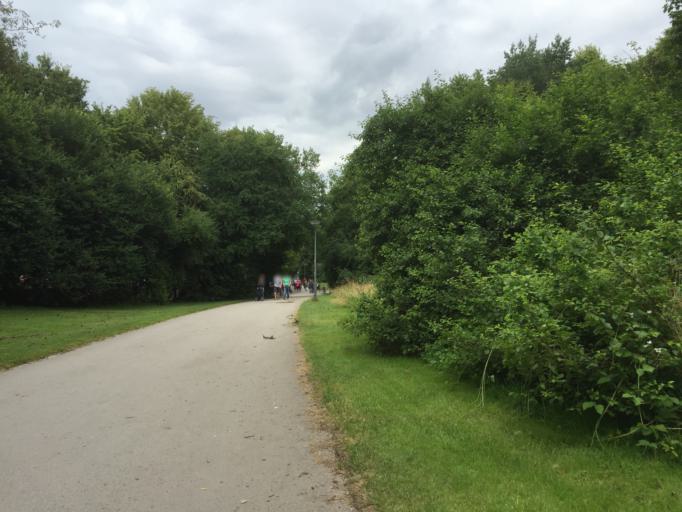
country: DE
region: Bavaria
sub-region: Upper Bavaria
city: Neubiberg
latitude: 48.1141
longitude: 11.6378
